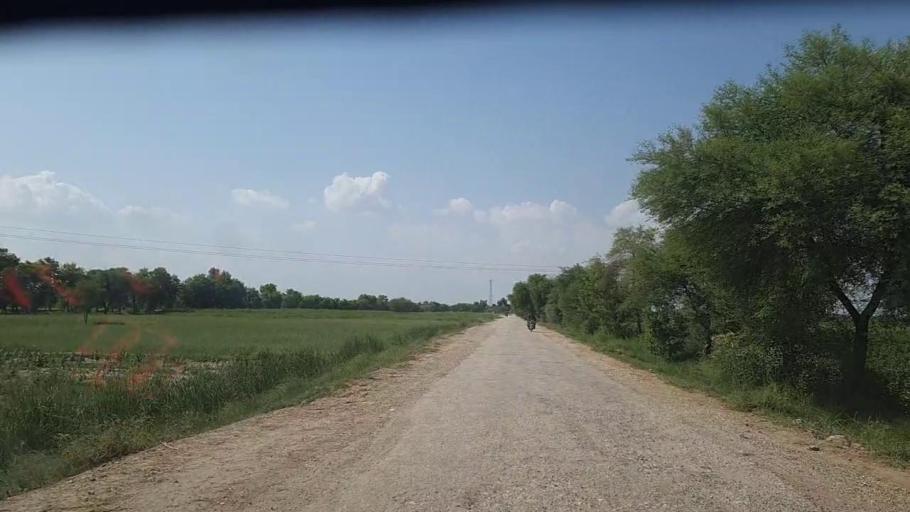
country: PK
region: Sindh
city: Khairpur
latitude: 28.1128
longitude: 69.6195
